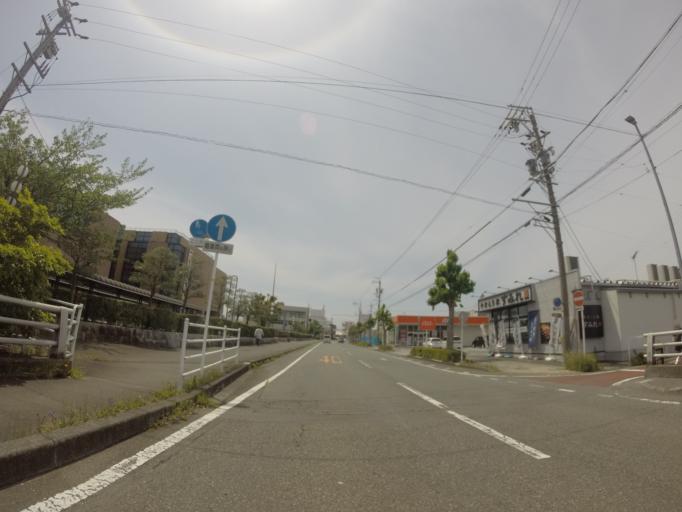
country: JP
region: Shizuoka
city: Yaizu
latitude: 34.8611
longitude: 138.3135
